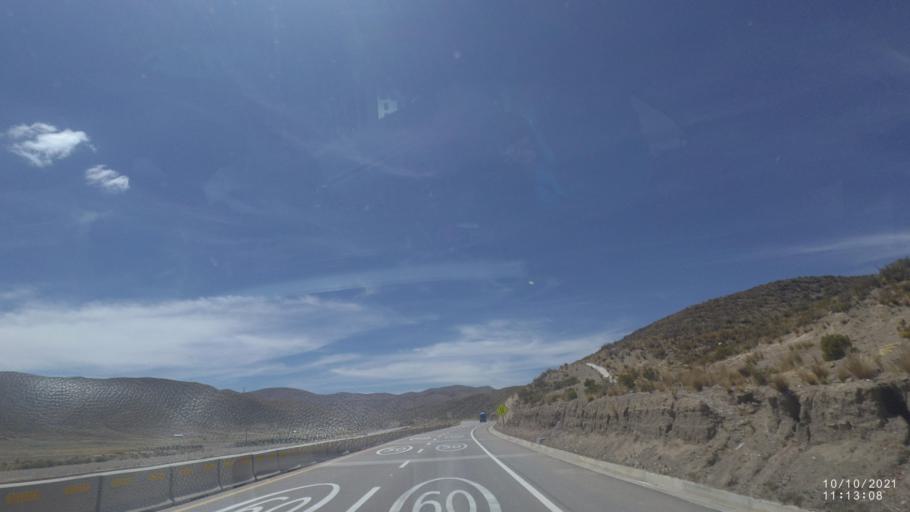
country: BO
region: La Paz
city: Colquiri
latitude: -17.6618
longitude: -67.0078
